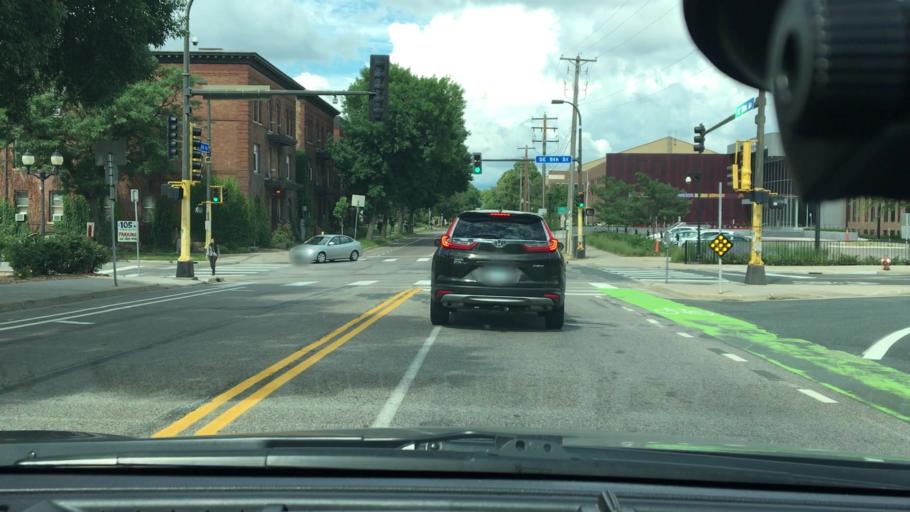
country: US
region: Minnesota
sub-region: Hennepin County
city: Minneapolis
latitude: 44.9807
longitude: -93.2339
